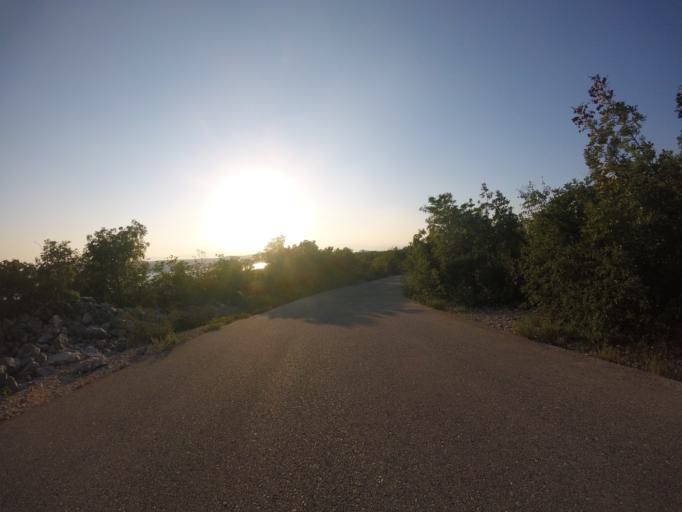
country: HR
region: Primorsko-Goranska
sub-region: Grad Crikvenica
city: Jadranovo
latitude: 45.2137
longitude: 14.6348
